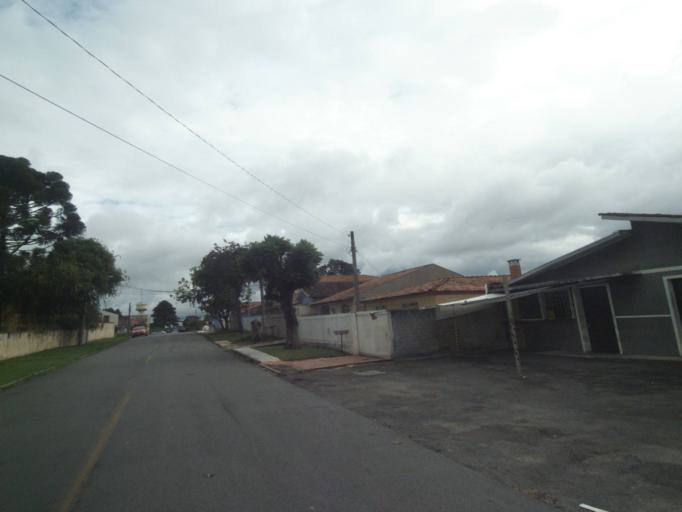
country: BR
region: Parana
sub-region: Curitiba
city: Curitiba
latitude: -25.4965
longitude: -49.3074
